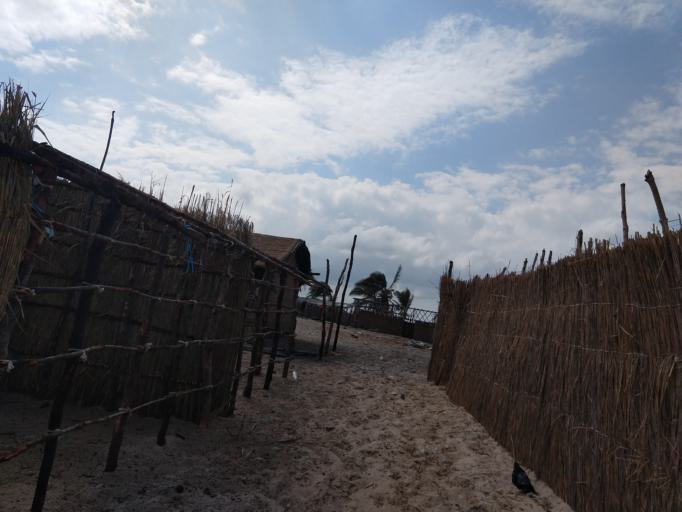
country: MZ
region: Sofala
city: Beira
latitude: -19.6498
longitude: 35.1786
